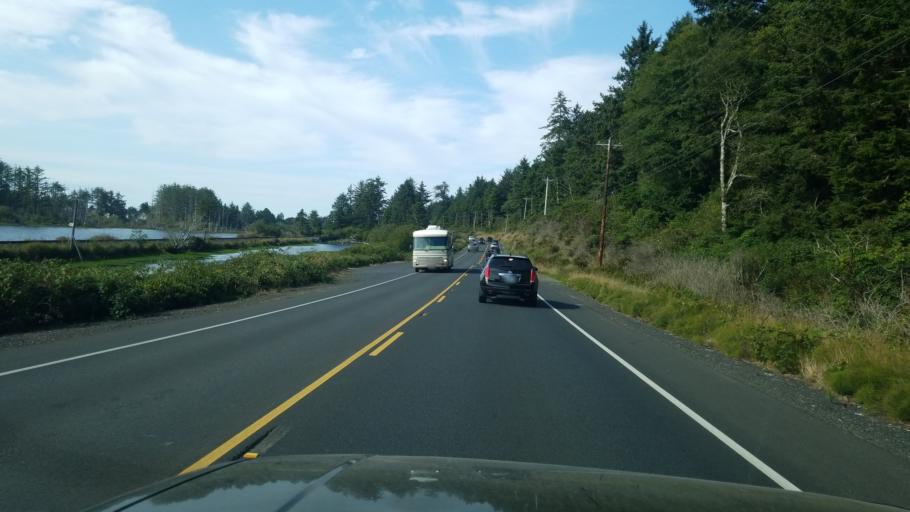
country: US
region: Oregon
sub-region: Tillamook County
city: Rockaway Beach
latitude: 45.5791
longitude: -123.9454
